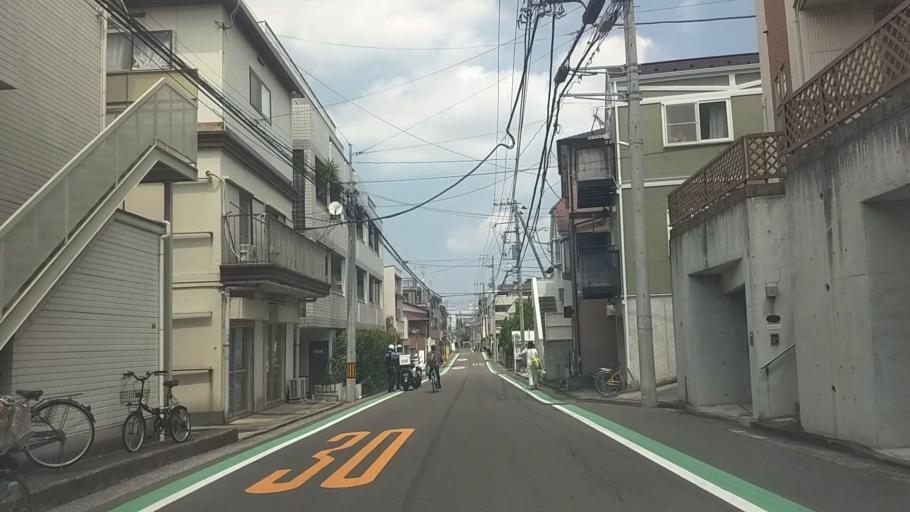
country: JP
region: Kanagawa
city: Yokohama
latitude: 35.5038
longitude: 139.6349
